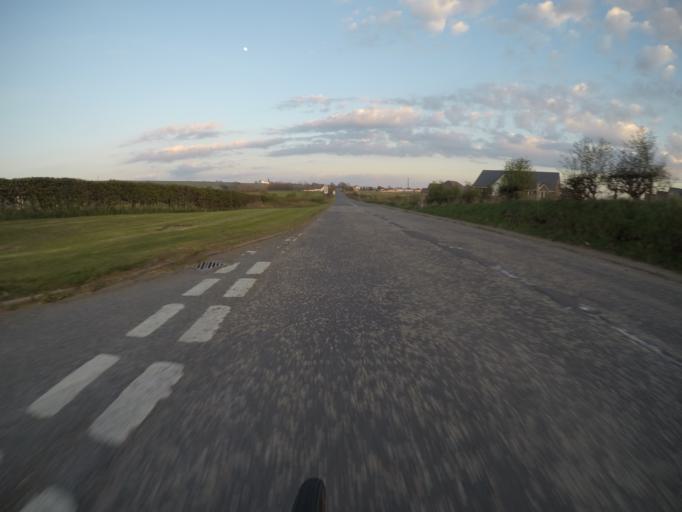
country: GB
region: Scotland
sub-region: South Ayrshire
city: Troon
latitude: 55.5624
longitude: -4.6339
